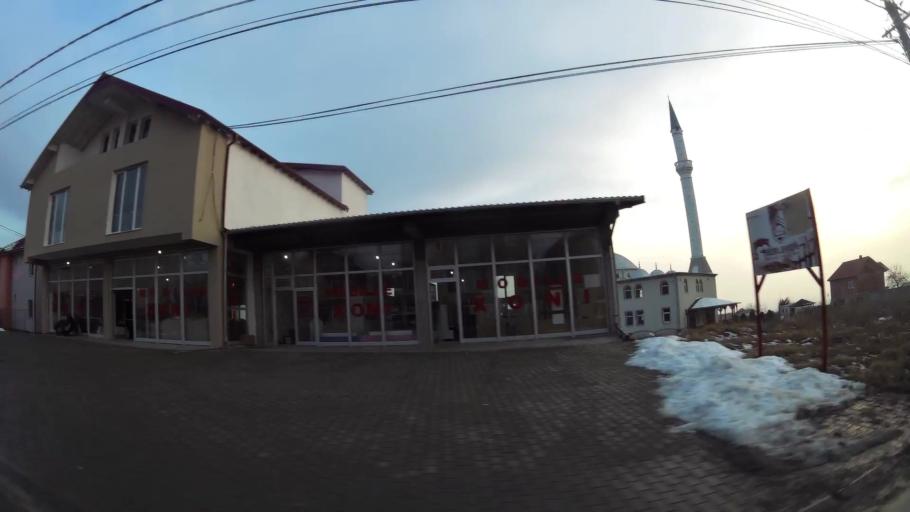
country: MK
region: Aracinovo
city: Arachinovo
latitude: 42.0276
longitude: 21.5761
